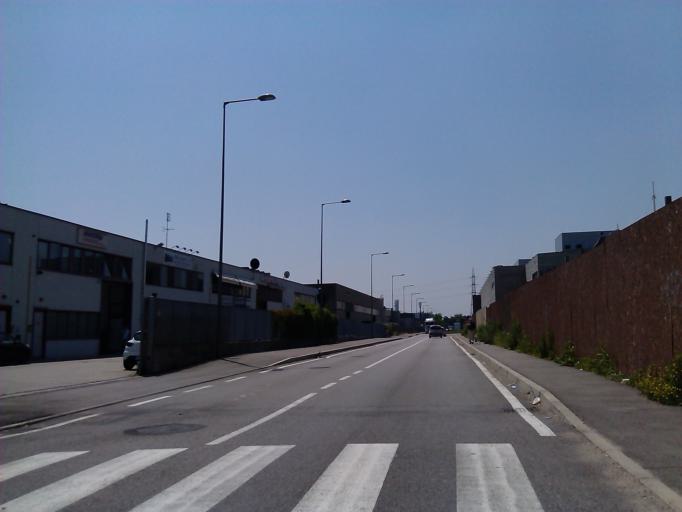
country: IT
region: Veneto
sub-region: Provincia di Venezia
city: Mestre
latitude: 45.4616
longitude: 12.2136
